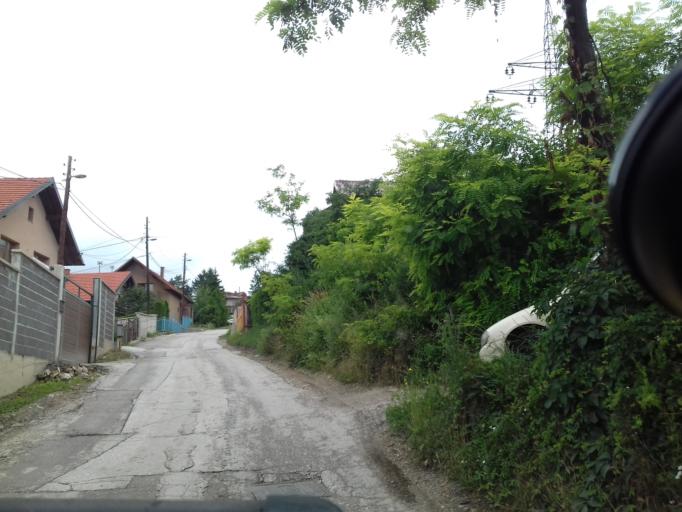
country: BA
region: Federation of Bosnia and Herzegovina
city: Zenica
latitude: 44.1985
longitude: 17.9275
